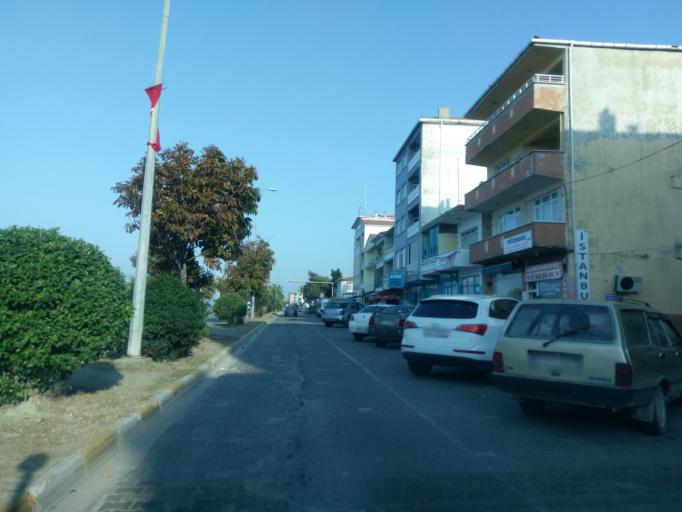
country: TR
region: Kastamonu
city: Catalzeytin
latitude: 41.9542
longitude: 34.2151
